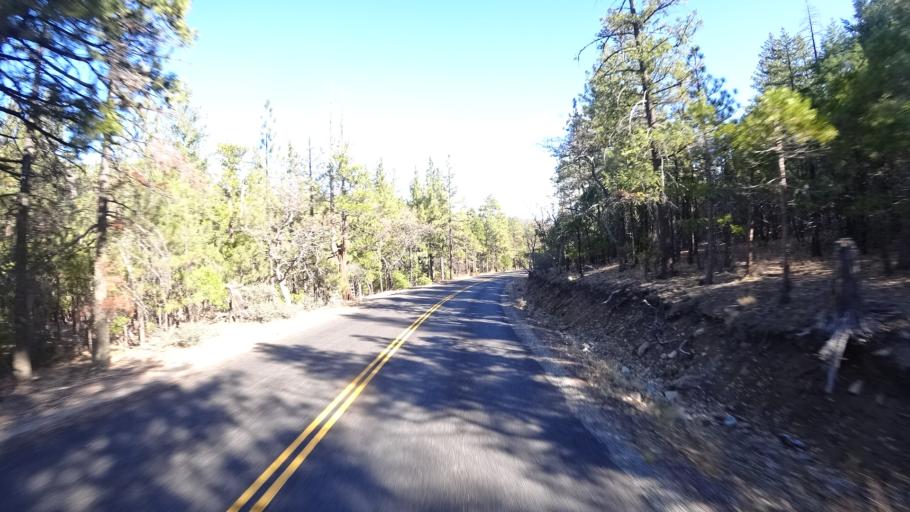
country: US
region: California
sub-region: Siskiyou County
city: Weed
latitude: 41.4322
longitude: -122.4950
